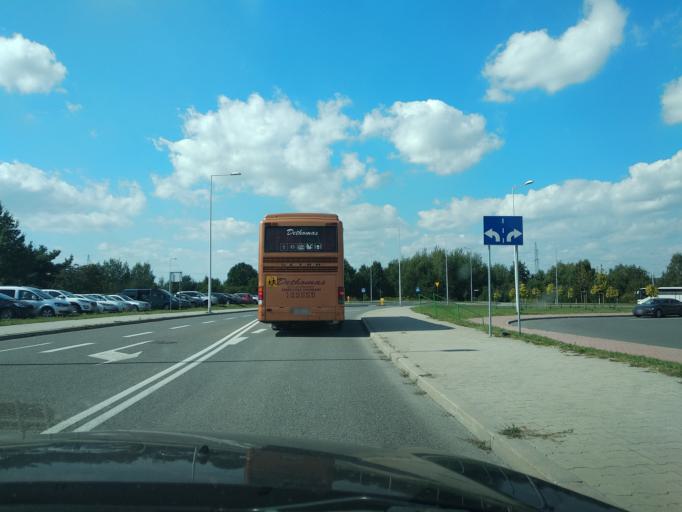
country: PL
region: Swietokrzyskie
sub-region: Powiat kielecki
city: Kostomloty Pierwsze
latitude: 50.9003
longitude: 20.5827
